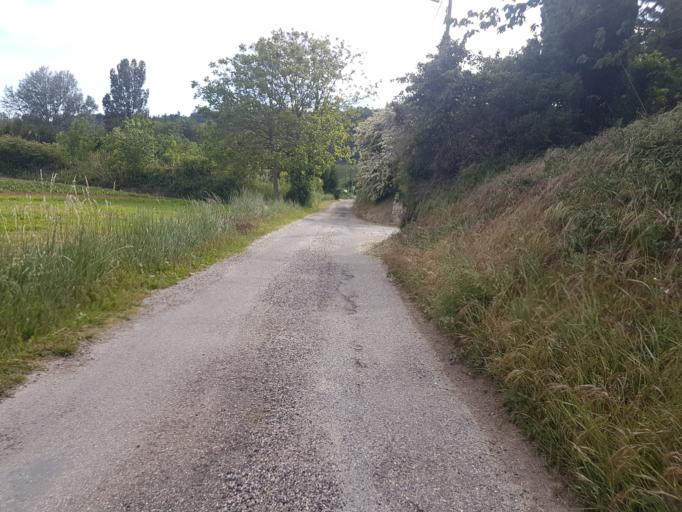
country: FR
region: Rhone-Alpes
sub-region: Departement de l'Ardeche
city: Guilherand-Granges
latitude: 44.9144
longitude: 4.8603
